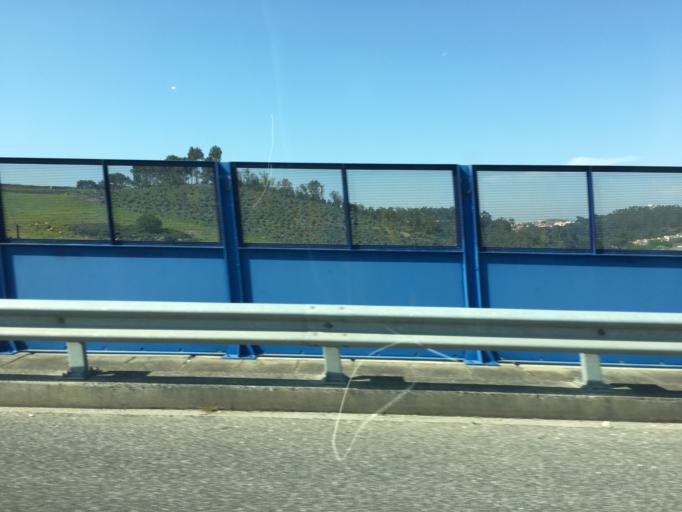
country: PT
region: Lisbon
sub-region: Sintra
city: Rio de Mouro
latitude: 38.8018
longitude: -9.3074
